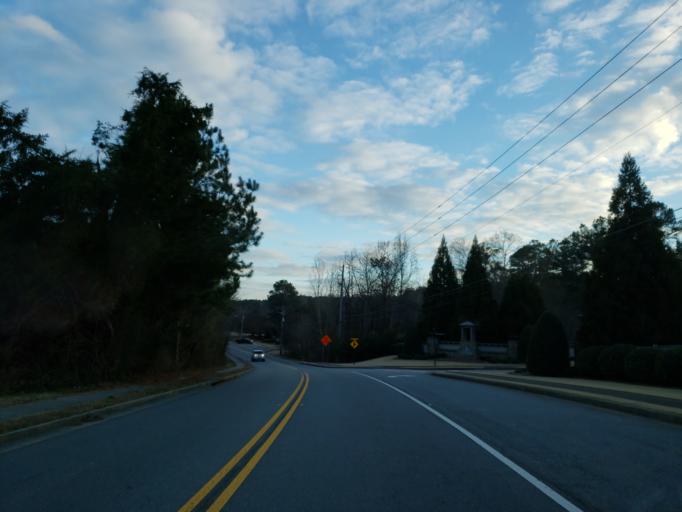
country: US
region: Georgia
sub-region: Cobb County
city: Acworth
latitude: 34.0071
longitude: -84.6795
